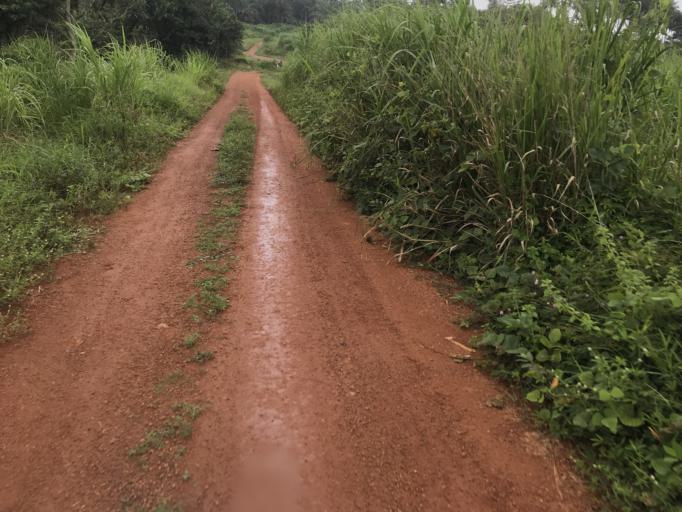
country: GN
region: Nzerekore
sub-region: Prefecture de Guekedou
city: Gueckedou
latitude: 8.4738
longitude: -10.2865
